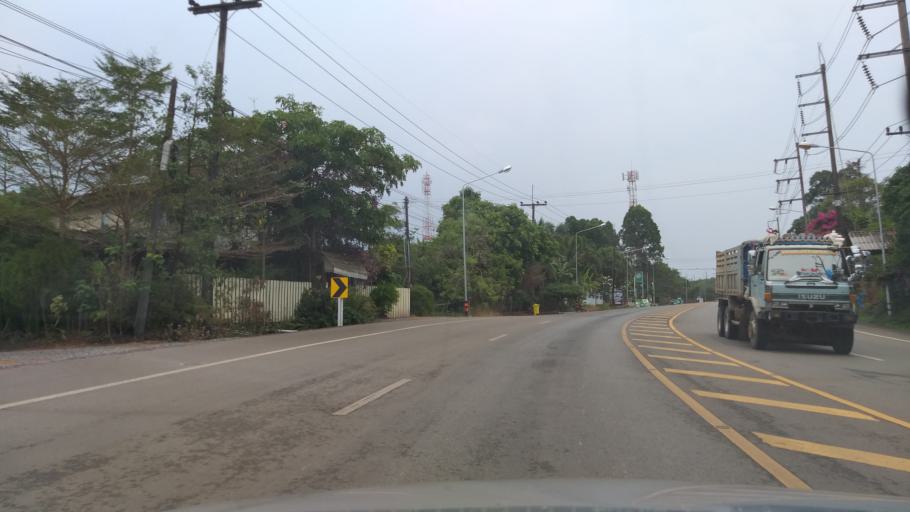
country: TH
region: Trat
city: Laem Ngop
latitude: 12.2587
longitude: 102.2871
